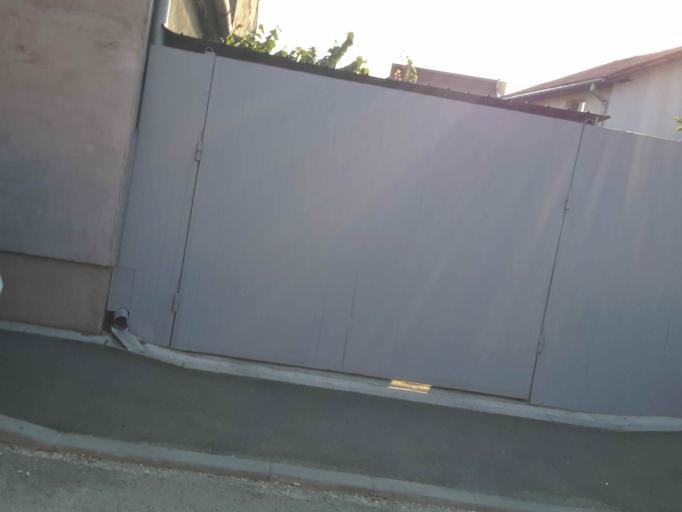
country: RO
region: Cluj
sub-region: Municipiul Cluj-Napoca
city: Cluj-Napoca
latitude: 46.7831
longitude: 23.6059
